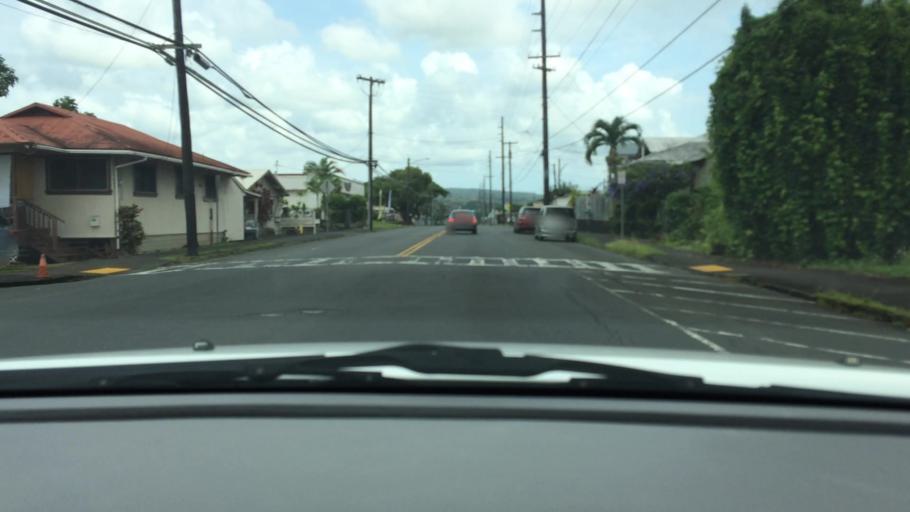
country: US
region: Hawaii
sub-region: Hawaii County
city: Hilo
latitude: 19.7139
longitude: -155.0818
